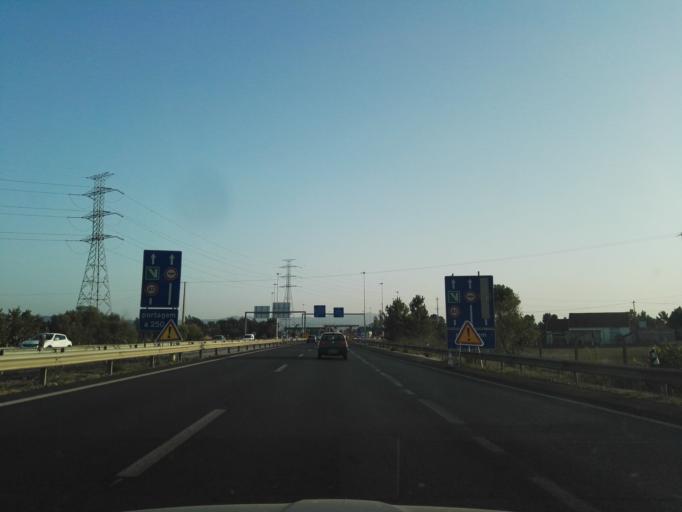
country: PT
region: Setubal
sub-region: Barreiro
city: Santo Antonio da Charneca
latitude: 38.5858
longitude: -9.0182
